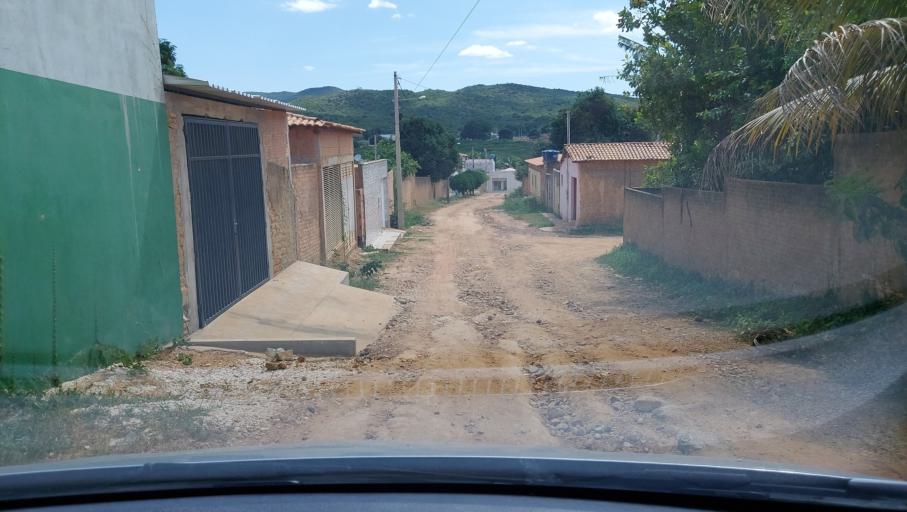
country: BR
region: Bahia
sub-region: Oliveira Dos Brejinhos
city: Beira Rio
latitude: -12.0033
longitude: -42.6274
